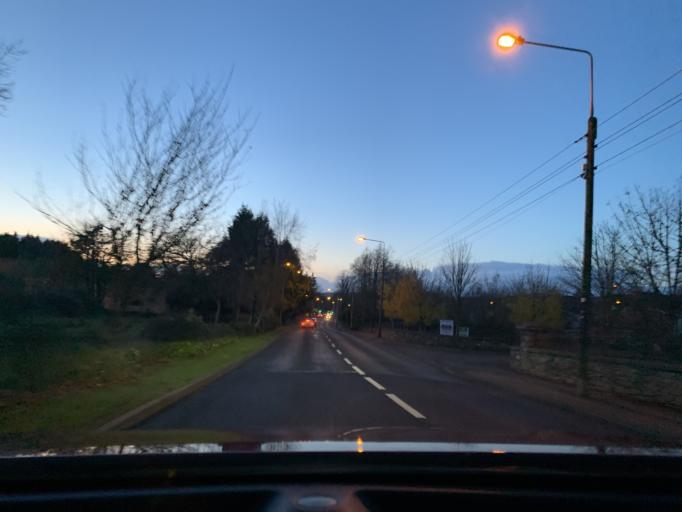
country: IE
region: Connaught
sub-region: Roscommon
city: Boyle
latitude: 53.9714
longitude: -8.2900
